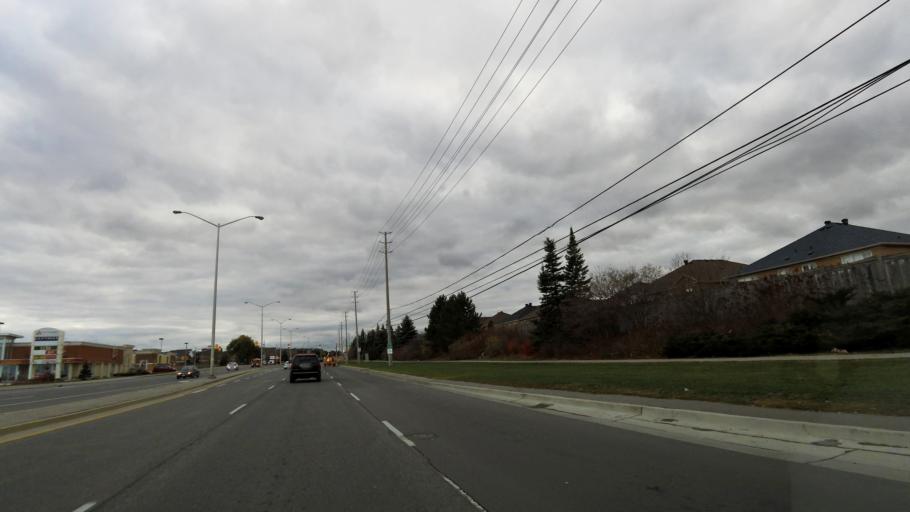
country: CA
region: Ontario
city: Brampton
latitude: 43.7622
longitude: -79.7238
